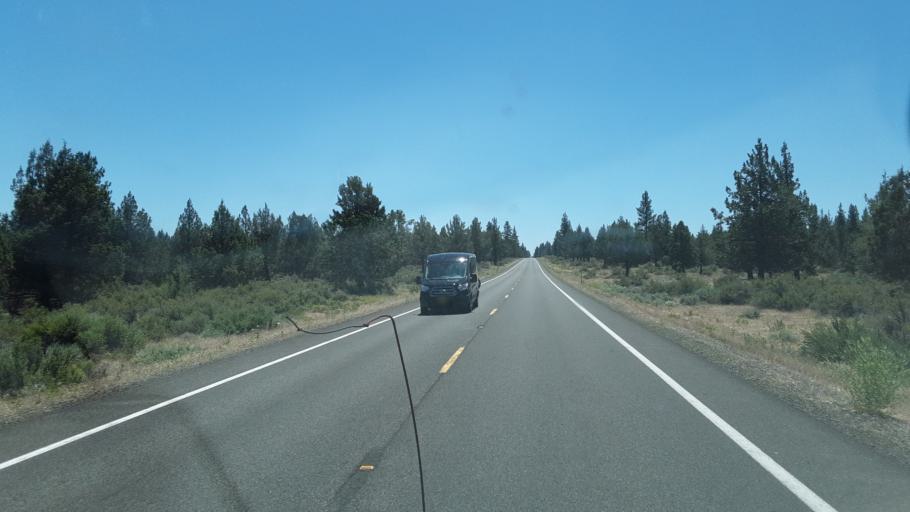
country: US
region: California
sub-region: Siskiyou County
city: Tulelake
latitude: 41.6379
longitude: -121.2325
